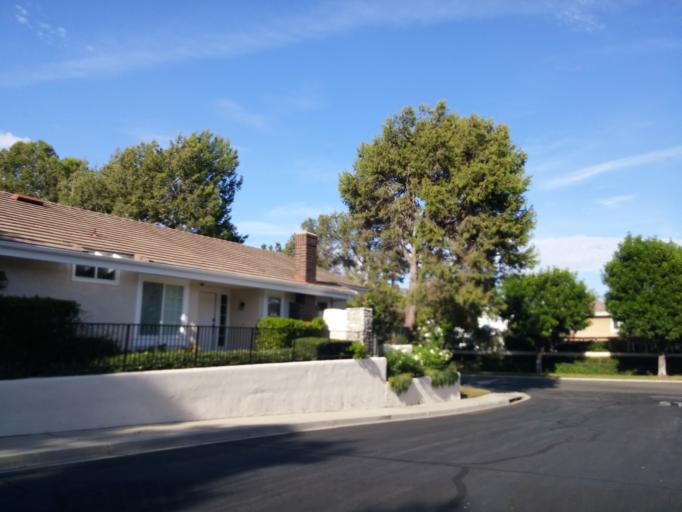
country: US
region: California
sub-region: Orange County
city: Irvine
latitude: 33.6684
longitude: -117.8028
